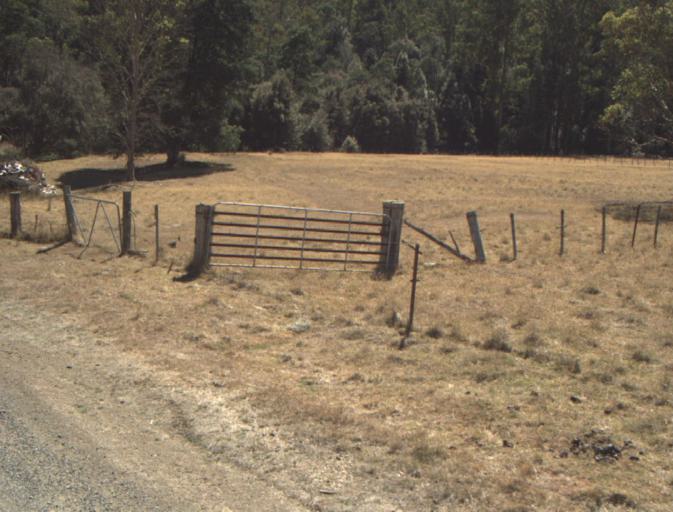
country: AU
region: Tasmania
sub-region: Dorset
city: Scottsdale
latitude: -41.2887
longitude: 147.3410
